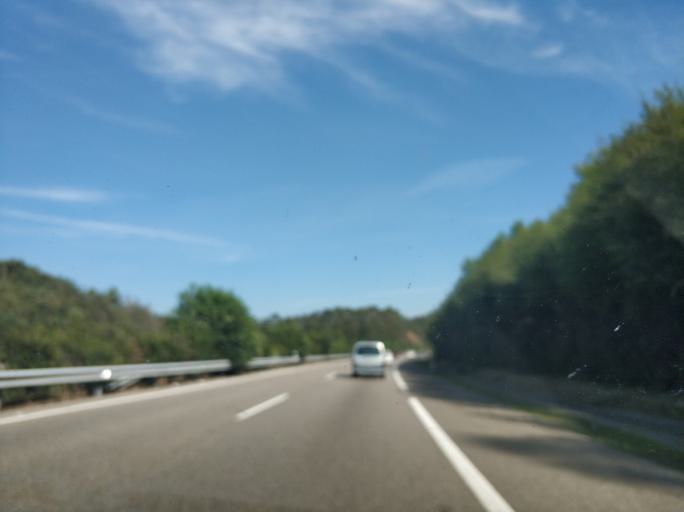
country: ES
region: Asturias
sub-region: Province of Asturias
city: Castrillon
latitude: 43.5467
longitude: -5.9706
